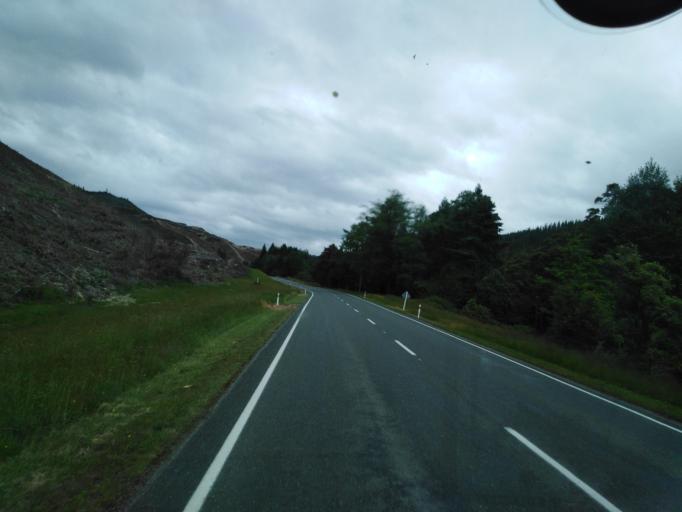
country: NZ
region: Tasman
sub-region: Tasman District
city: Wakefield
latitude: -41.5867
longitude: 172.7652
